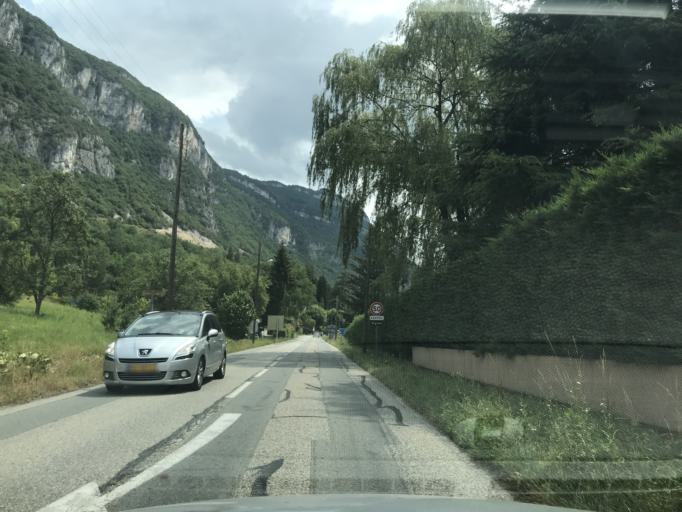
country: FR
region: Rhone-Alpes
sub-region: Departement de la Savoie
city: Chindrieux
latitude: 45.8096
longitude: 5.8517
